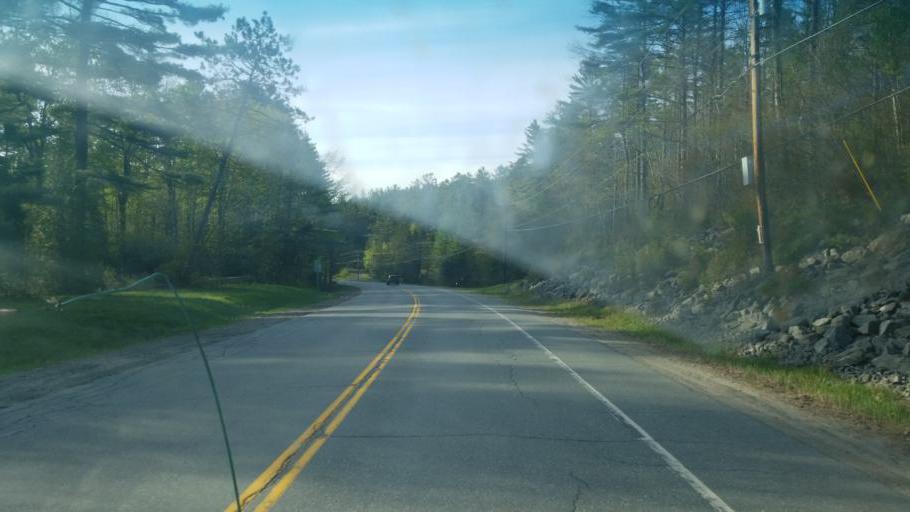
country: US
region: New Hampshire
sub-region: Grafton County
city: Littleton
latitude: 44.3219
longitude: -71.8036
